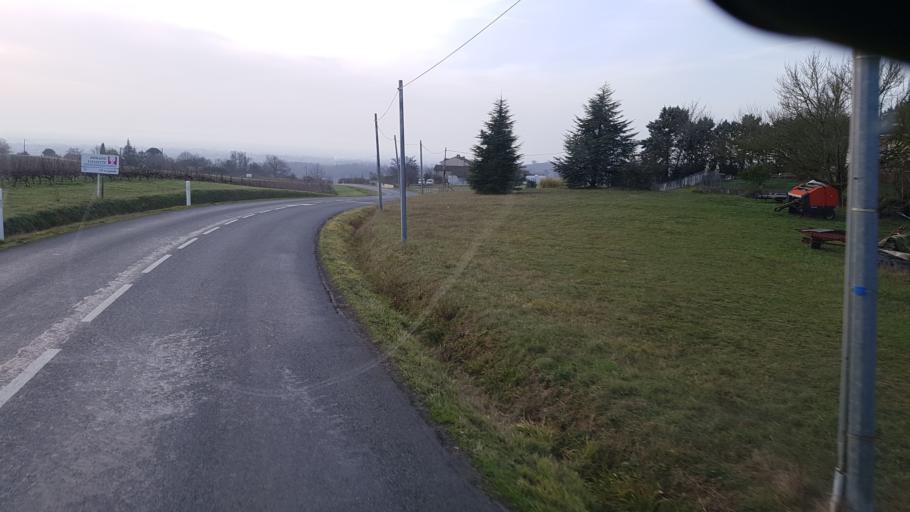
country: FR
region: Midi-Pyrenees
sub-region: Departement du Tarn
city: Cahuzac-sur-Vere
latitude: 43.9456
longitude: 1.8845
